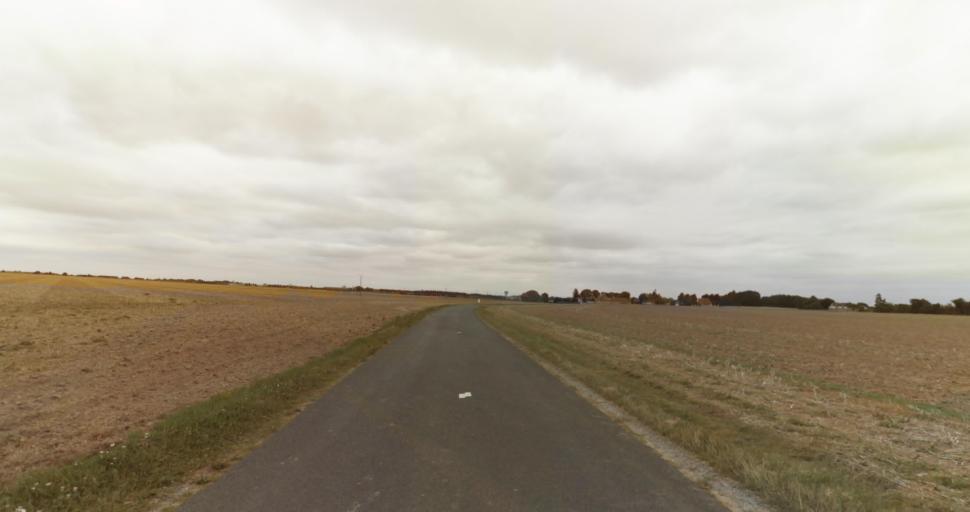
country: FR
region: Haute-Normandie
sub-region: Departement de l'Eure
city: Evreux
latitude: 49.0012
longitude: 1.2044
